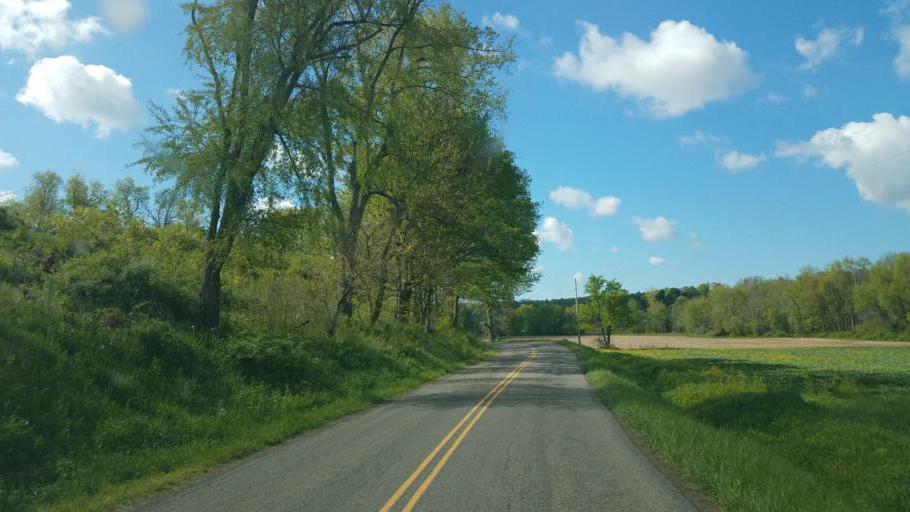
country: US
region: Ohio
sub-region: Knox County
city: Danville
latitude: 40.4970
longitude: -82.3558
